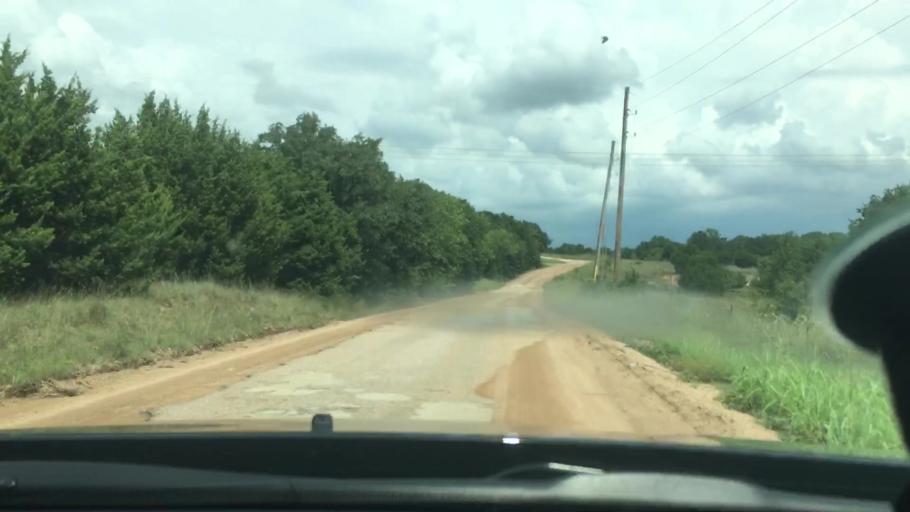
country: US
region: Oklahoma
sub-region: Carter County
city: Dickson
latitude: 34.2469
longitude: -96.9288
